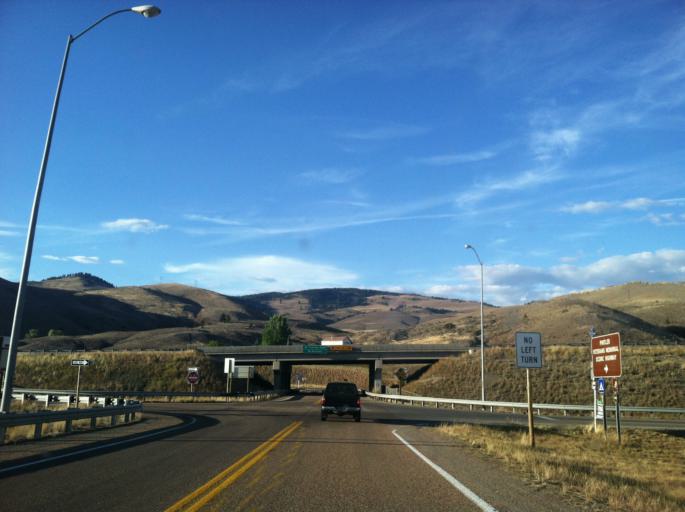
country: US
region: Montana
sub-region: Granite County
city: Philipsburg
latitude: 46.6710
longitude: -113.1537
